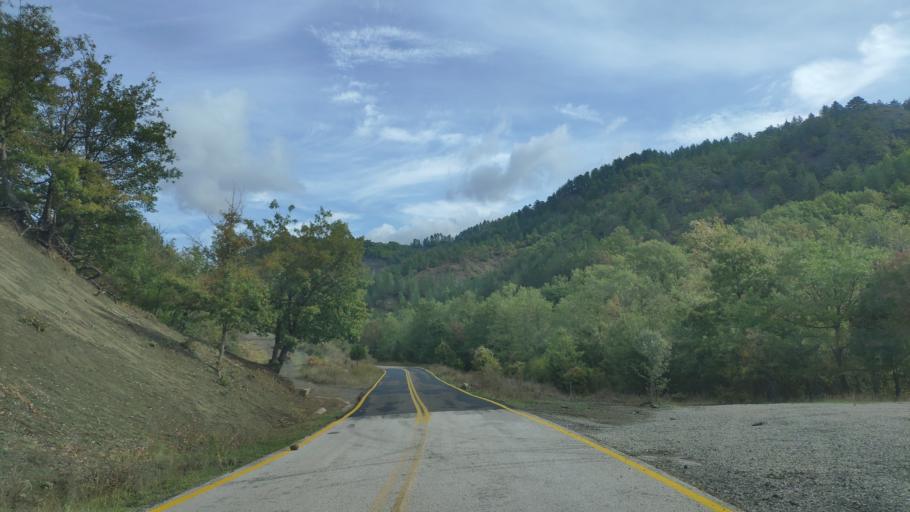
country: GR
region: West Macedonia
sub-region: Nomos Kastorias
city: Nestorio
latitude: 40.2335
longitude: 20.9883
